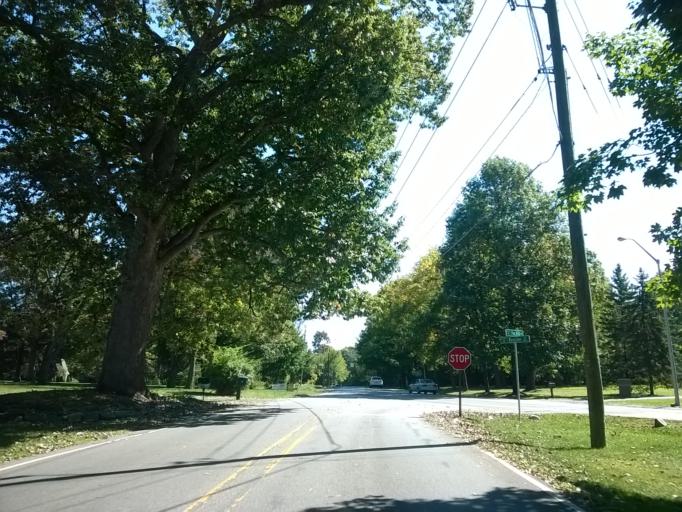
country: US
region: Indiana
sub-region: Marion County
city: Broad Ripple
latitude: 39.8629
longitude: -86.1690
